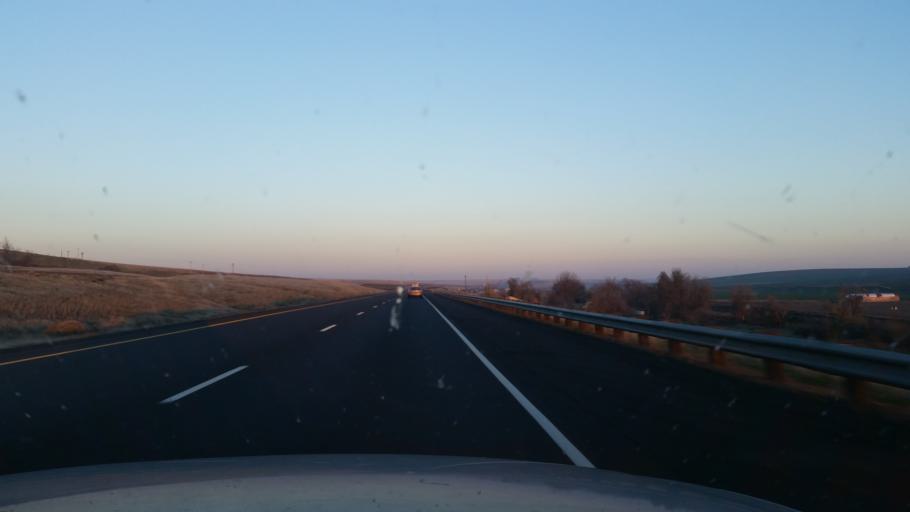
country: US
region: Washington
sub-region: Grant County
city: Warden
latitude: 47.0844
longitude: -118.9465
